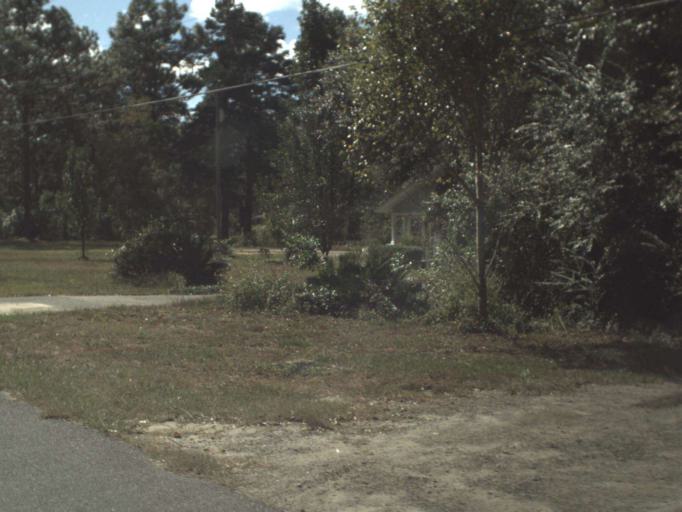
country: US
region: Florida
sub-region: Washington County
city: Chipley
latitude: 30.7709
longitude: -85.5669
